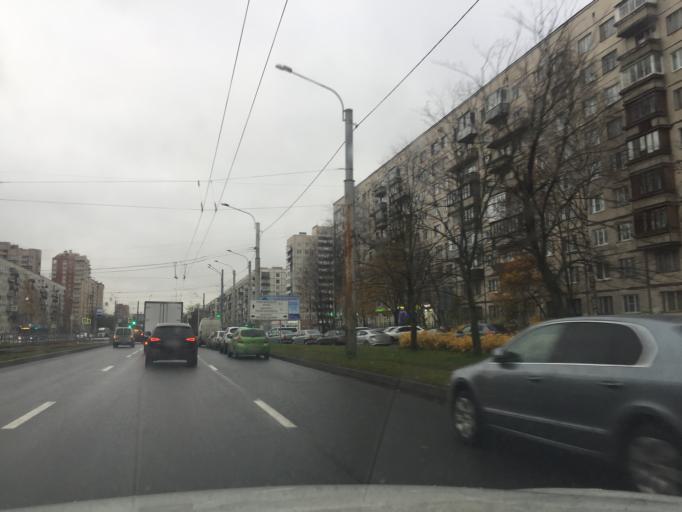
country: RU
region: St.-Petersburg
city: Grazhdanka
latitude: 60.0411
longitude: 30.3997
